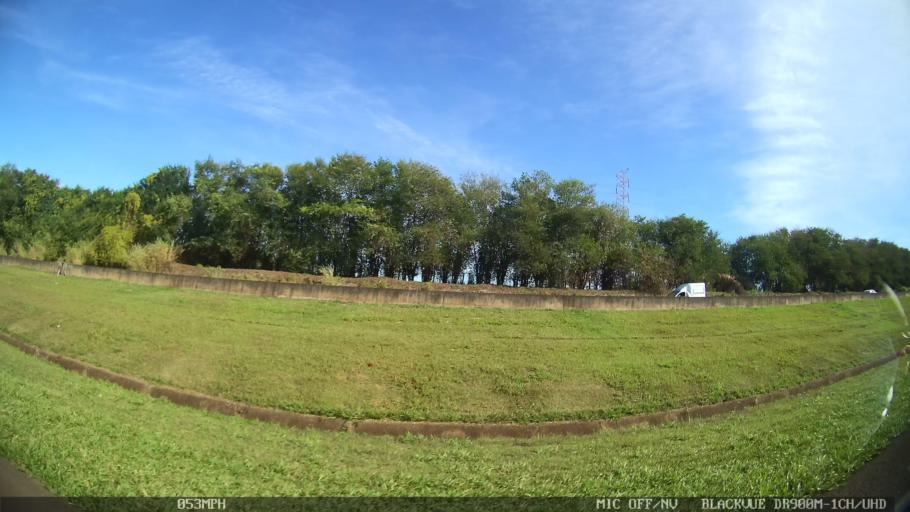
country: BR
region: Sao Paulo
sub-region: Leme
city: Leme
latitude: -22.2688
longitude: -47.3913
